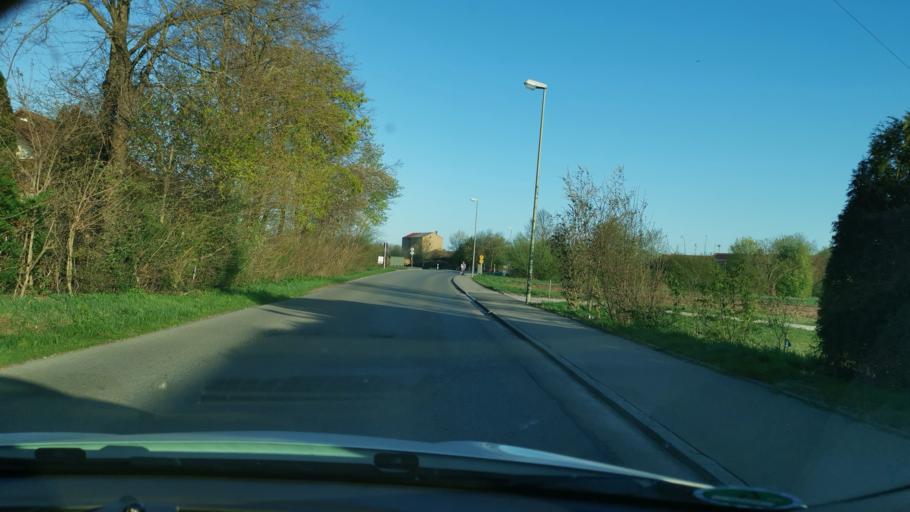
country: DE
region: Bavaria
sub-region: Swabia
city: Rehling
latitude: 48.4879
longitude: 10.9168
